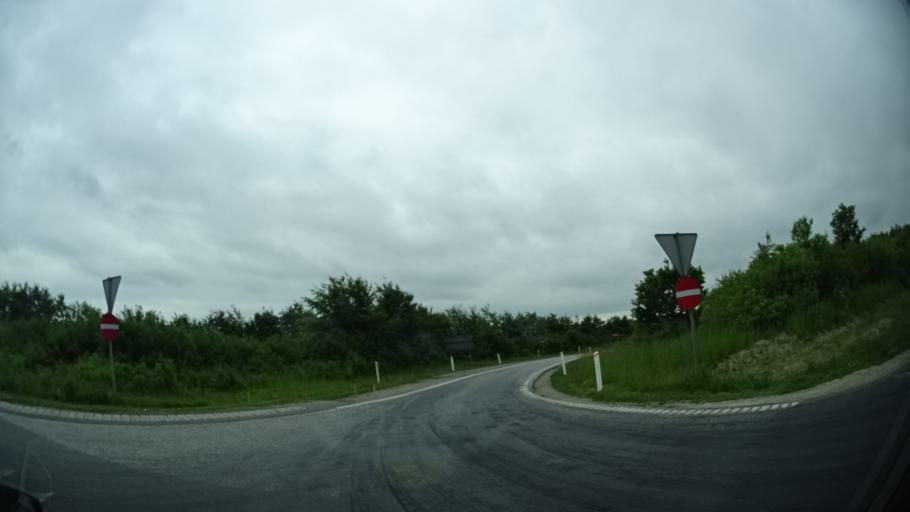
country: DK
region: Central Jutland
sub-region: Arhus Kommune
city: Kolt
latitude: 56.1072
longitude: 10.0549
